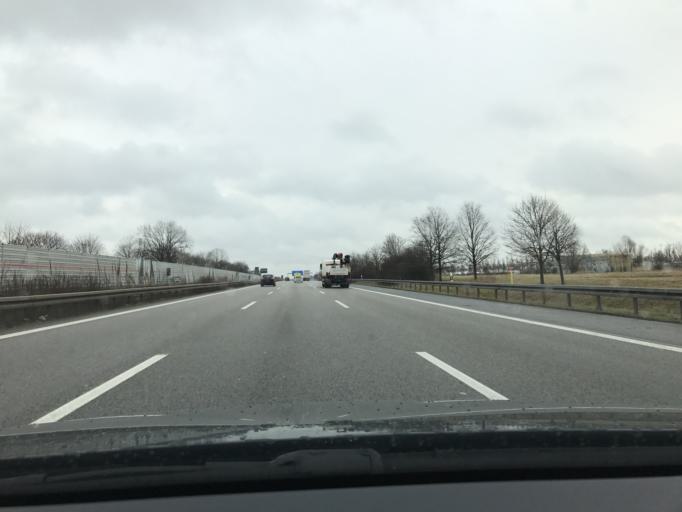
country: DE
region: Saxony
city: Rackwitz
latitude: 51.4013
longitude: 12.4070
